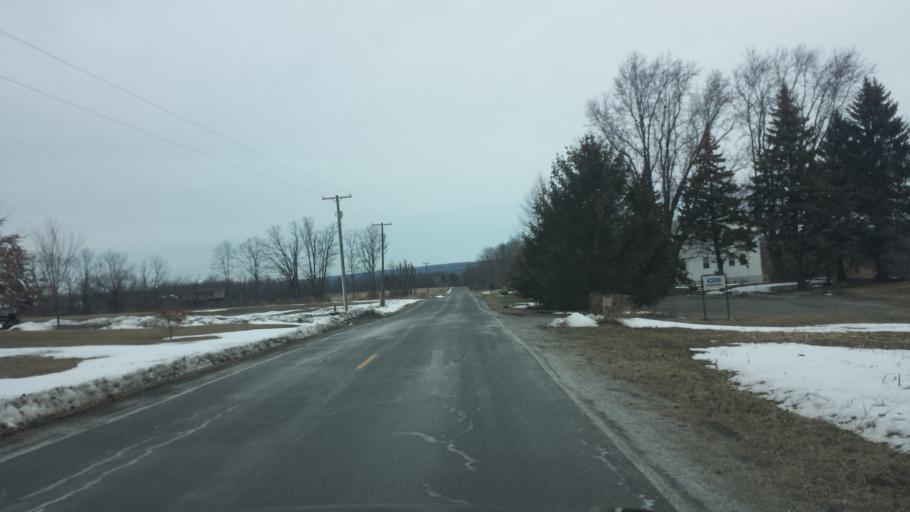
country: US
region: New York
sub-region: Tompkins County
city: Northwest Ithaca
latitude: 42.4932
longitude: -76.5739
